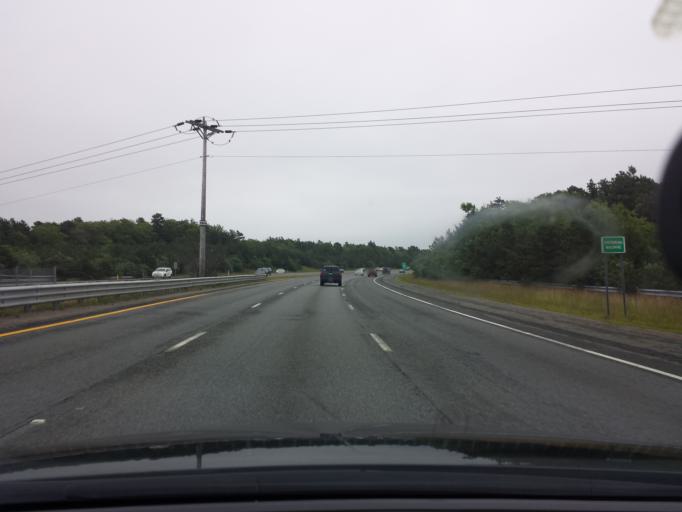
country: US
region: Massachusetts
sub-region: Barnstable County
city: Bourne
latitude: 41.7787
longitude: -70.5906
